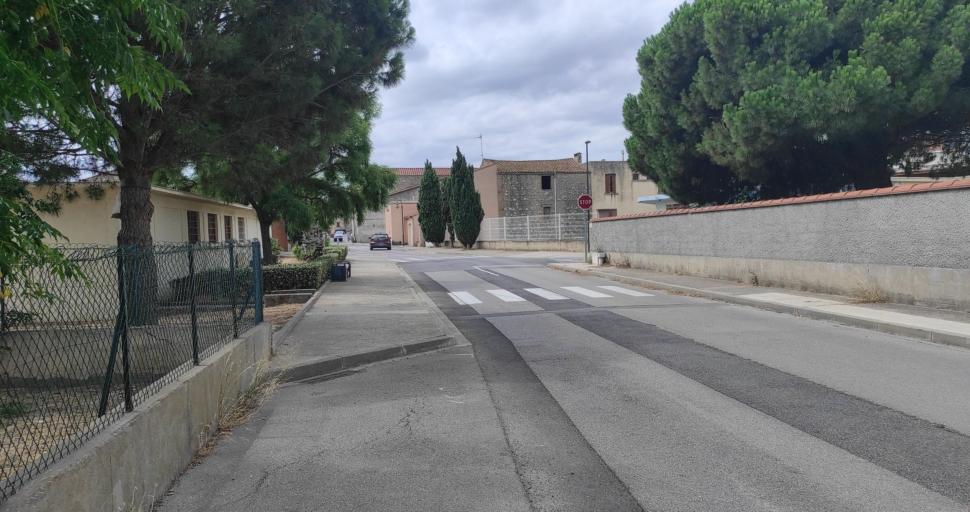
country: FR
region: Languedoc-Roussillon
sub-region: Departement des Pyrenees-Orientales
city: Saint-Hippolyte
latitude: 42.7869
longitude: 2.9680
